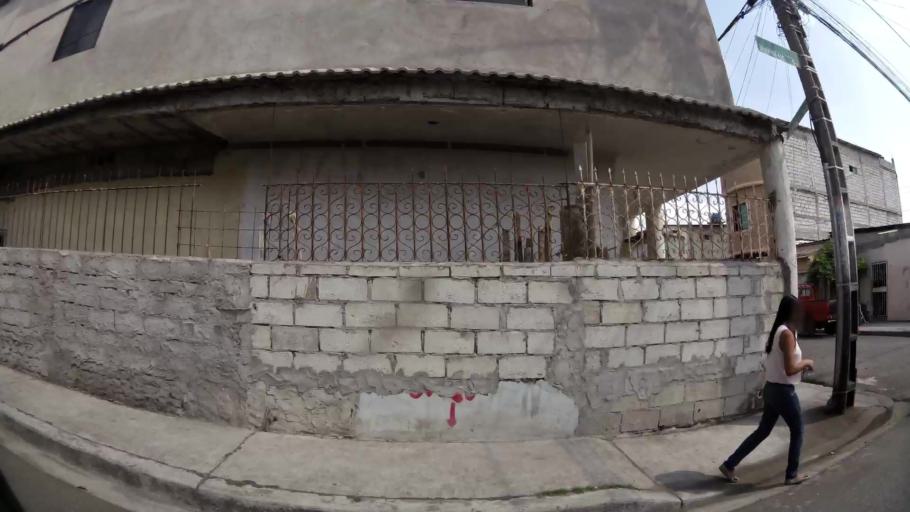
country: EC
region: Guayas
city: Guayaquil
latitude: -2.2607
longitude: -79.8833
